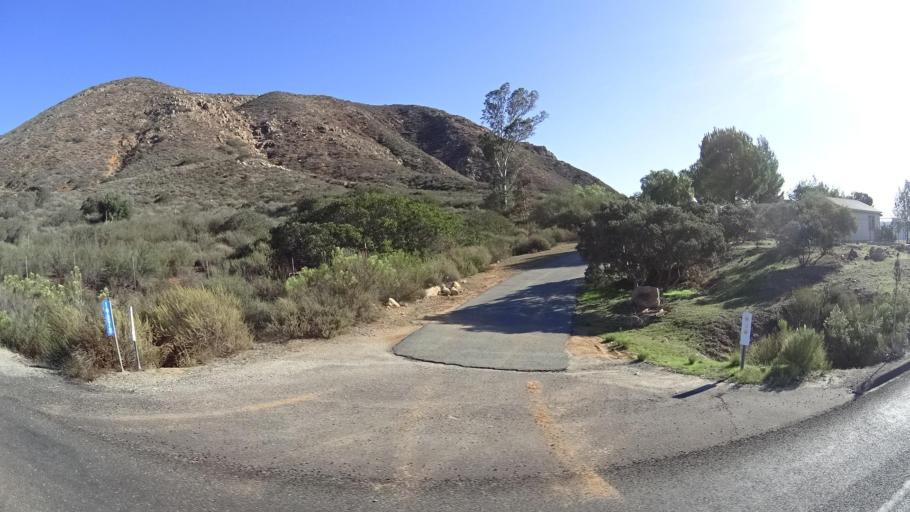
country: MX
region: Baja California
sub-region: Tijuana
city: Villa del Campo
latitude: 32.6173
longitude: -116.7386
